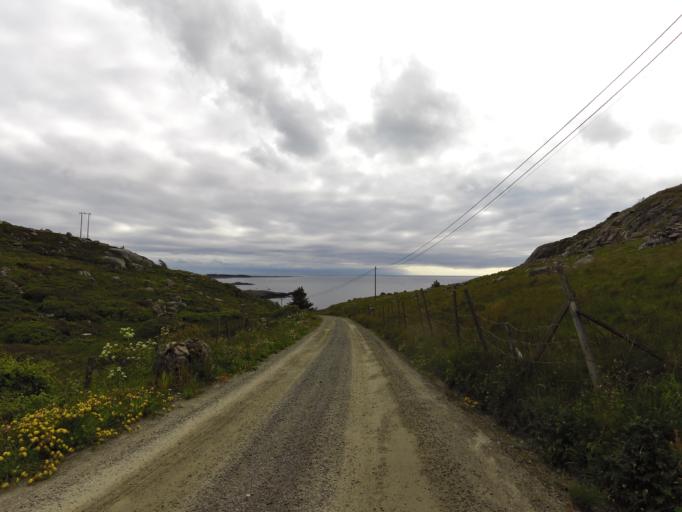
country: NO
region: Vest-Agder
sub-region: Farsund
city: Vestbygd
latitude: 58.1491
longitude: 6.6159
